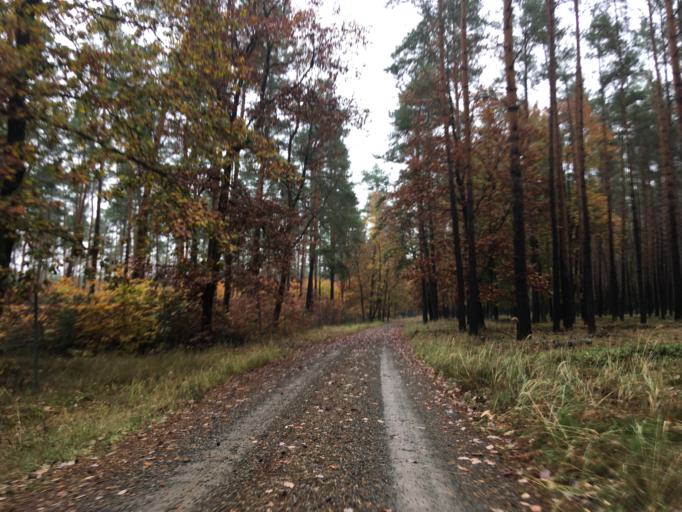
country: DE
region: Brandenburg
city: Beeskow
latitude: 52.2503
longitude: 14.2912
